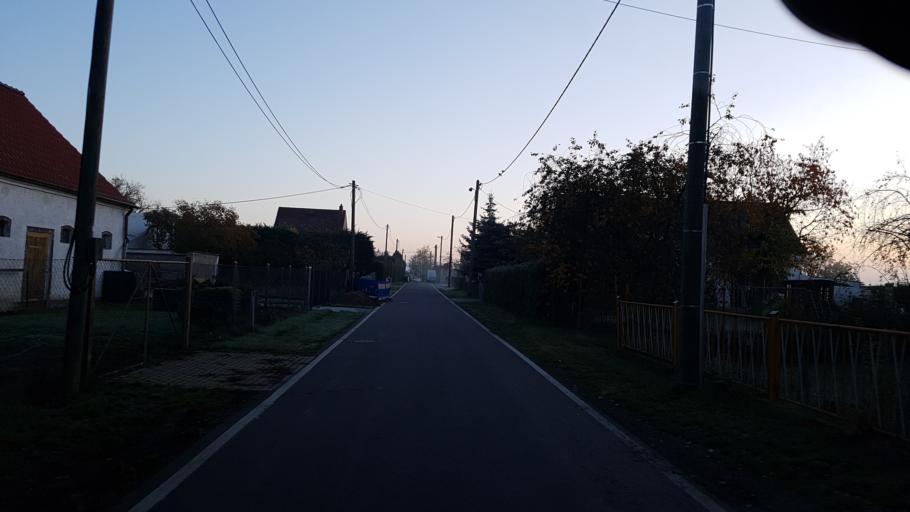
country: DE
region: Saxony
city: Arzberg
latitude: 51.5399
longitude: 13.1708
